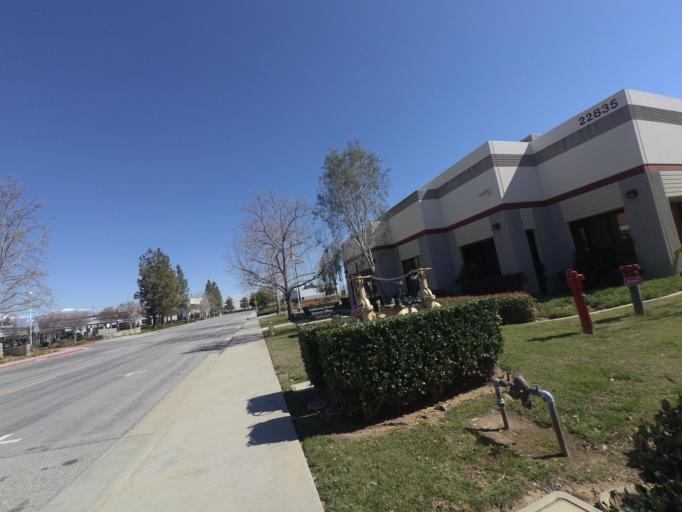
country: US
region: California
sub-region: Riverside County
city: March Air Force Base
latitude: 33.9143
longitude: -117.2637
